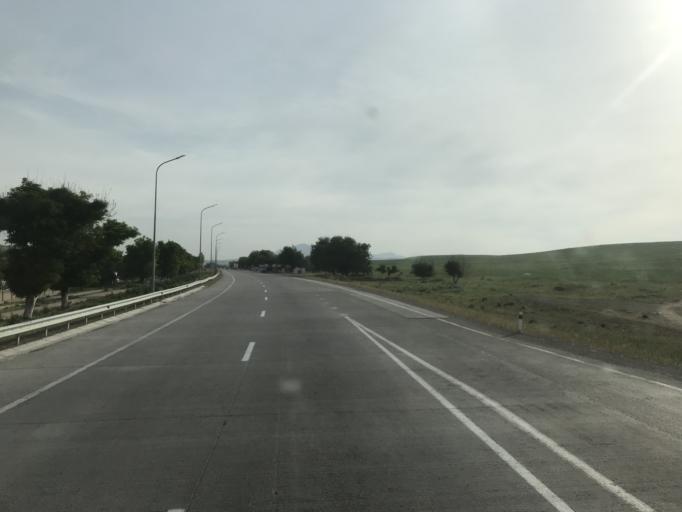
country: KZ
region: Ongtustik Qazaqstan
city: Qazyqurt
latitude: 41.9018
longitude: 69.4615
